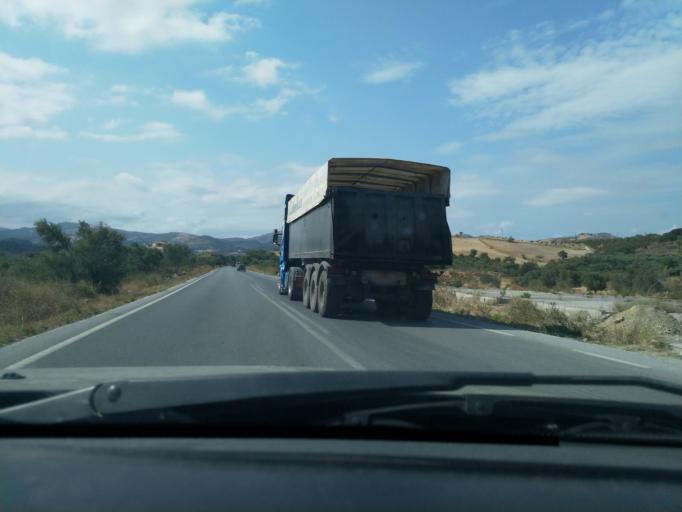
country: GR
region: Crete
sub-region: Nomos Rethymnis
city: Atsipopoulon
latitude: 35.2252
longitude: 24.4806
